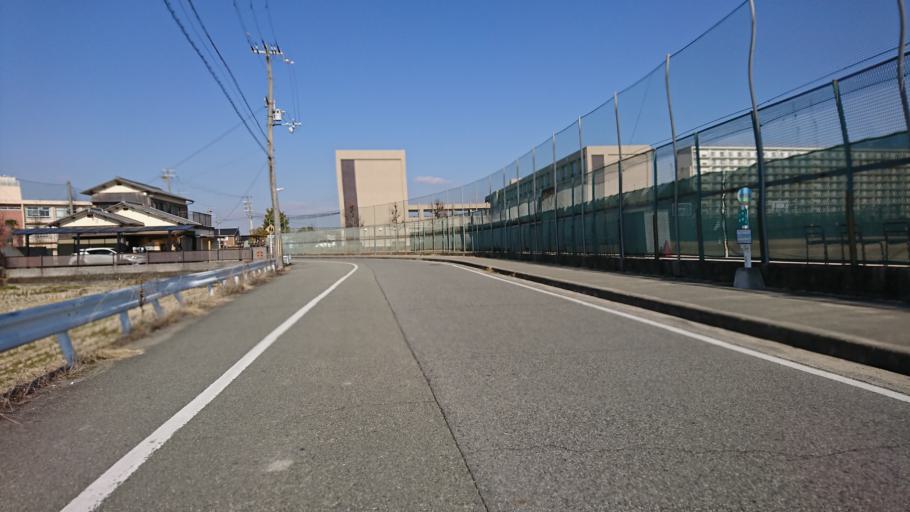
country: JP
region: Hyogo
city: Kakogawacho-honmachi
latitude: 34.7325
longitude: 134.8624
